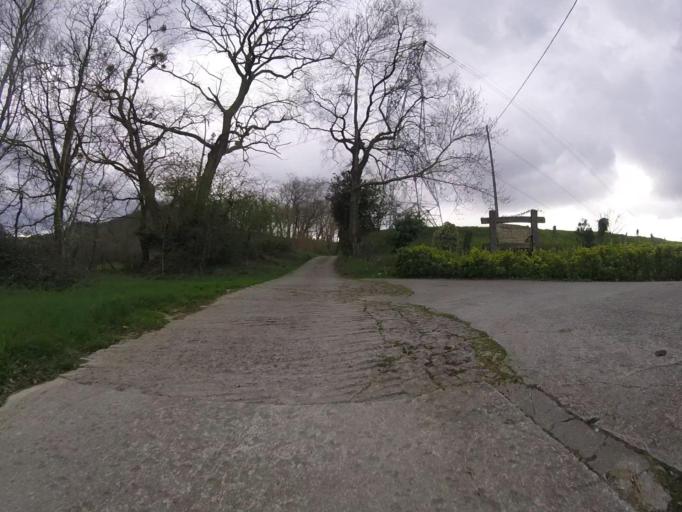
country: ES
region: Basque Country
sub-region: Provincia de Guipuzcoa
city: Errenteria
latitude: 43.2800
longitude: -1.8624
